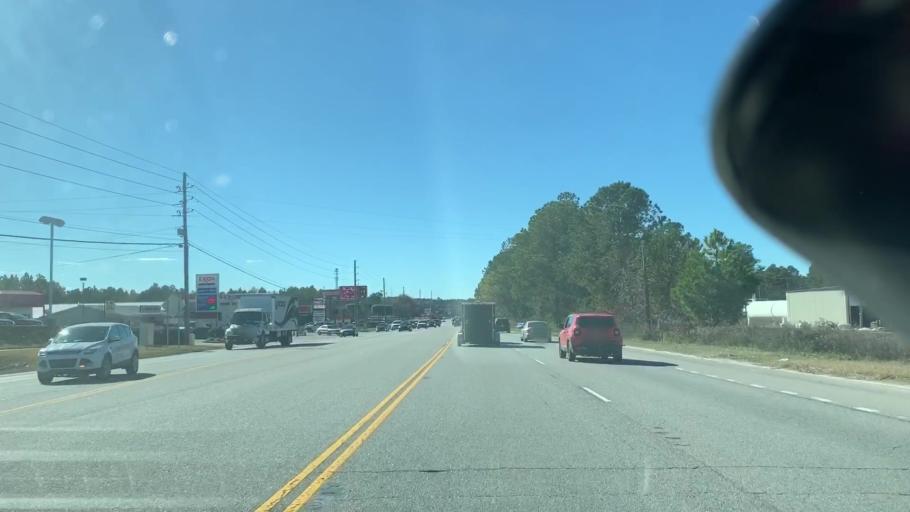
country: US
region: South Carolina
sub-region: Richland County
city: Woodfield
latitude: 34.1111
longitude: -80.8962
